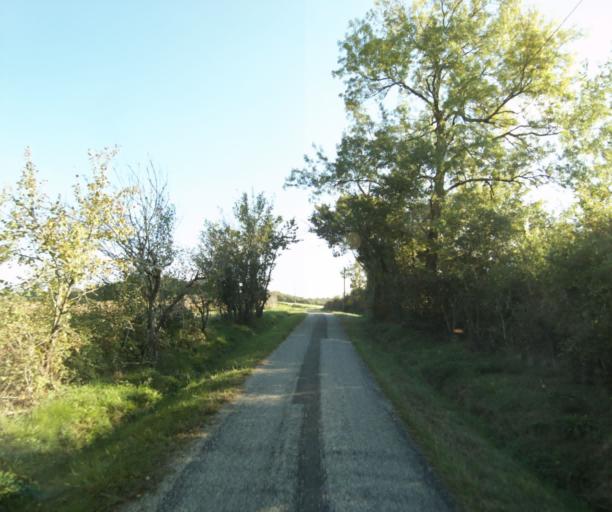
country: FR
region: Midi-Pyrenees
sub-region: Departement du Gers
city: Eauze
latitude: 43.7891
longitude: 0.1198
